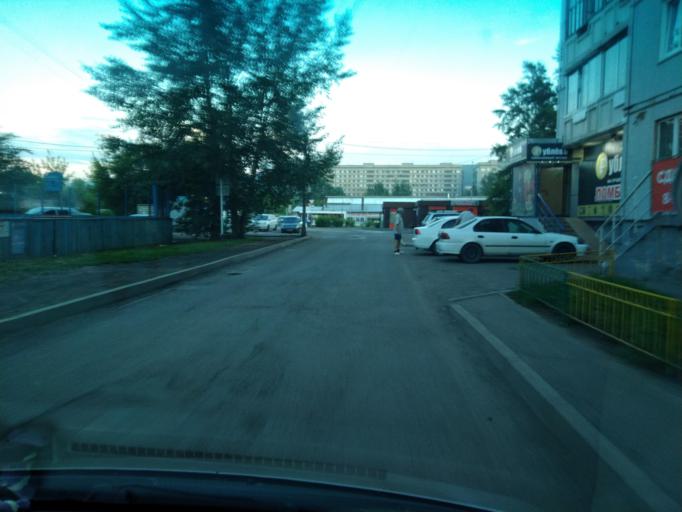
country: RU
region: Krasnoyarskiy
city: Krasnoyarsk
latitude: 55.9864
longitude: 92.8703
